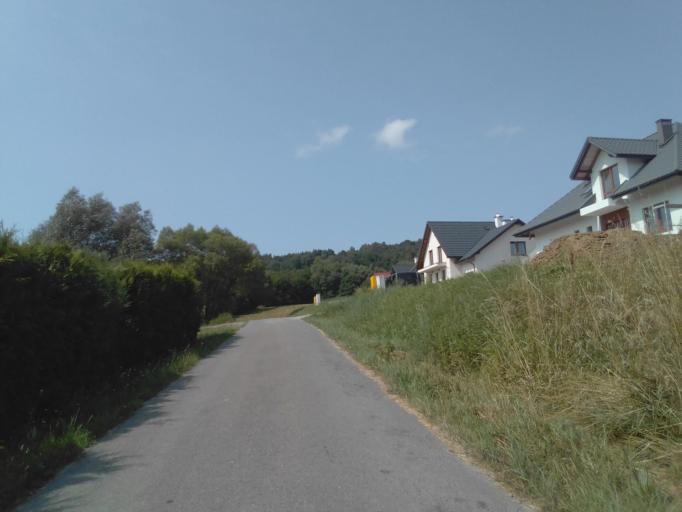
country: PL
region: Subcarpathian Voivodeship
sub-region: Powiat brzozowski
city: Domaradz
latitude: 49.7888
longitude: 21.9375
